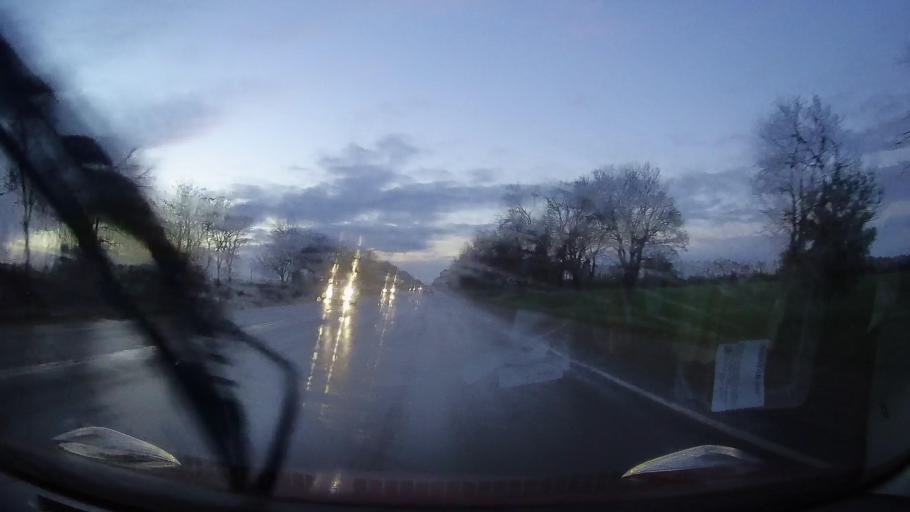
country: RU
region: Krasnodarskiy
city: Zavetnyy
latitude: 44.8880
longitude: 41.2127
